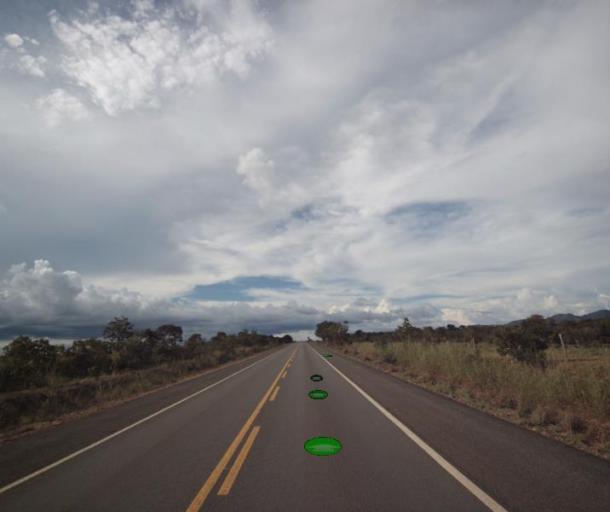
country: BR
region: Goias
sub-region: Niquelandia
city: Niquelandia
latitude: -14.7190
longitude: -48.6077
